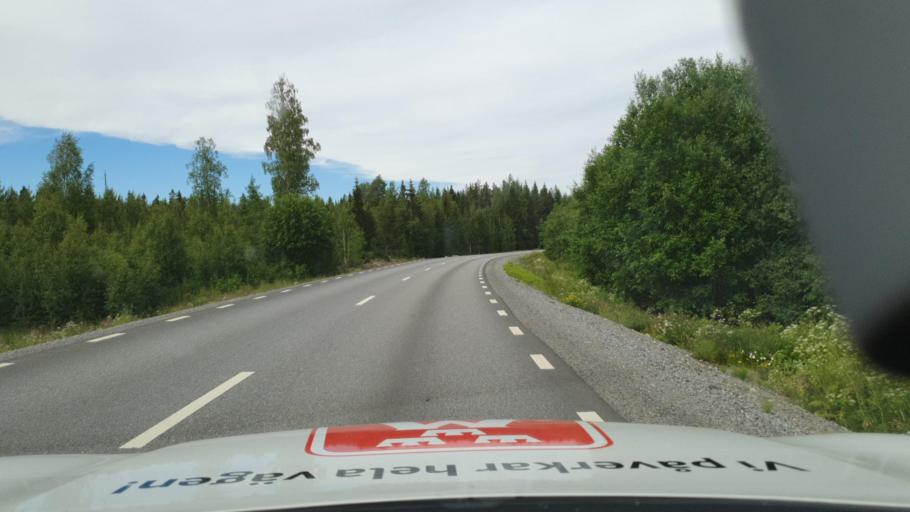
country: SE
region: Vaesterbotten
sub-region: Skelleftea Kommun
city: Burtraesk
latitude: 64.5010
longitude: 20.6253
